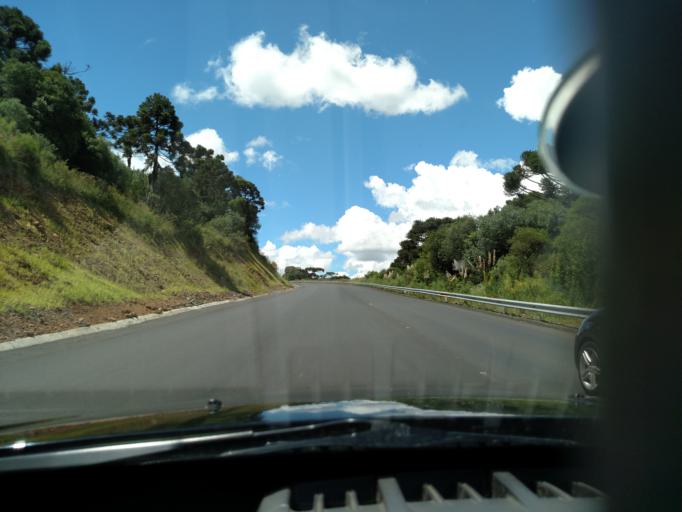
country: BR
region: Santa Catarina
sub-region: Sao Joaquim
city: Sao Joaquim
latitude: -28.2472
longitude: -49.9716
